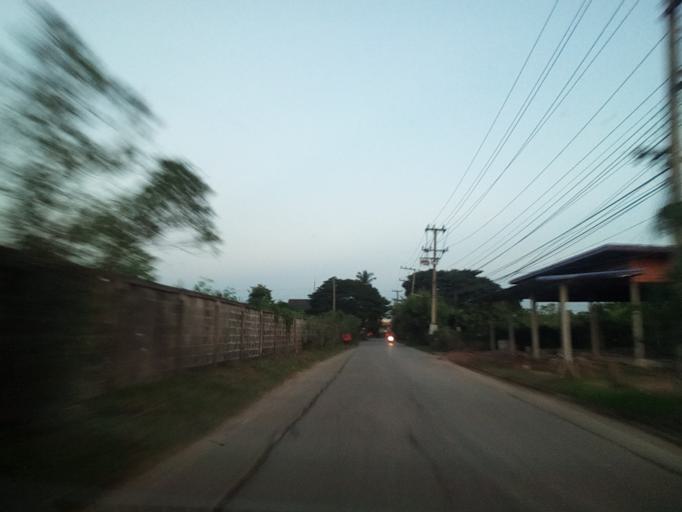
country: TH
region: Lamphun
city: Ban Thi
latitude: 18.6350
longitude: 99.0487
